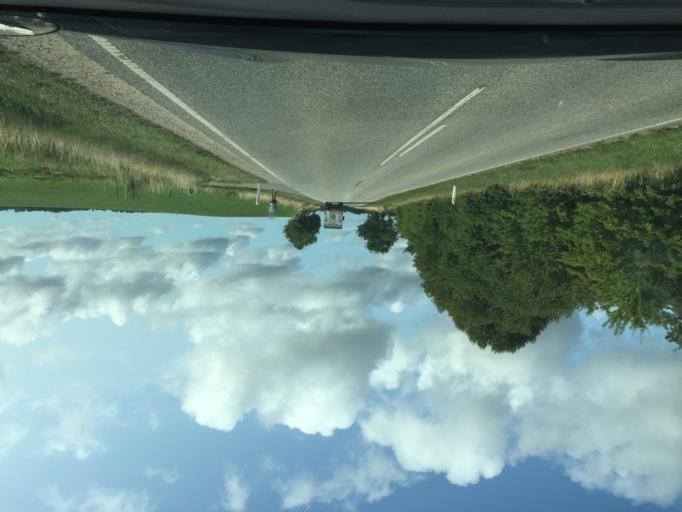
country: DK
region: Central Jutland
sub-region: Odder Kommune
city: Odder
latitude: 55.9003
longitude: 10.0206
